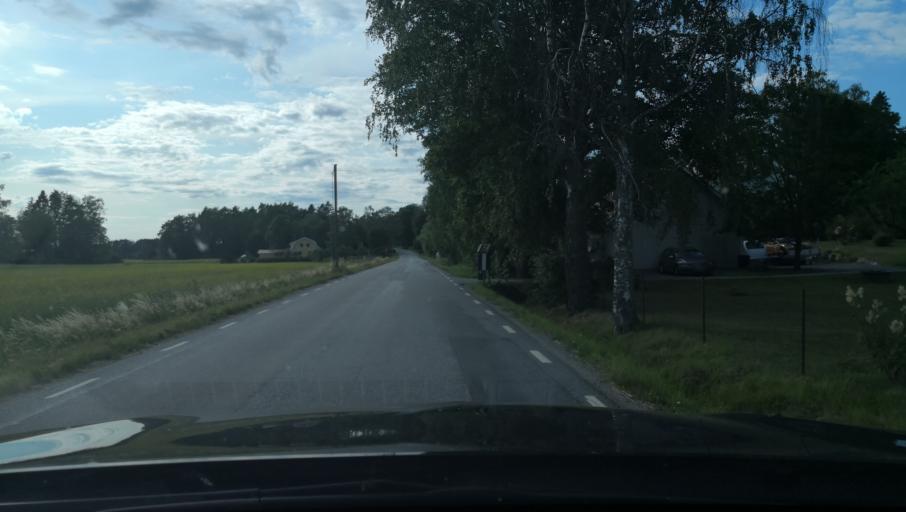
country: SE
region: Uppsala
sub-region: Enkopings Kommun
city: Orsundsbro
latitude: 59.6868
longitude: 17.3911
